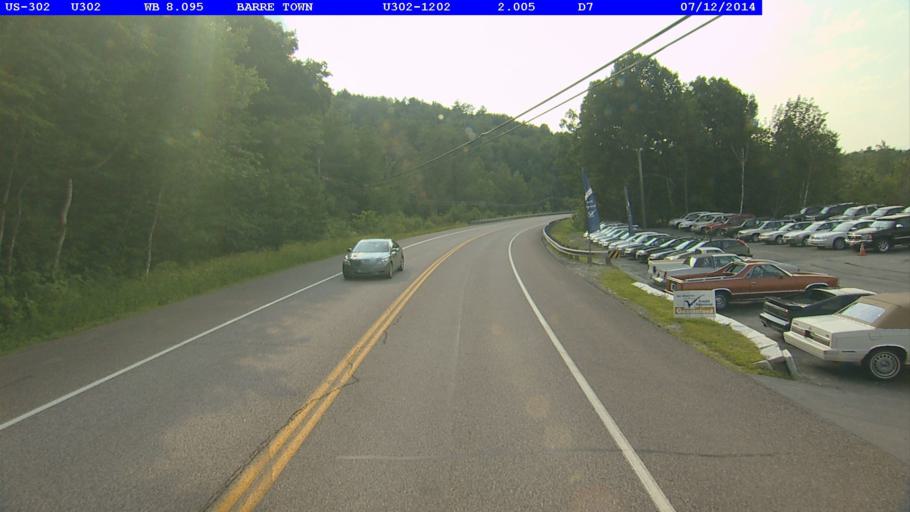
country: US
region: Vermont
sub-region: Washington County
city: South Barre
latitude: 44.1660
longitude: -72.4564
